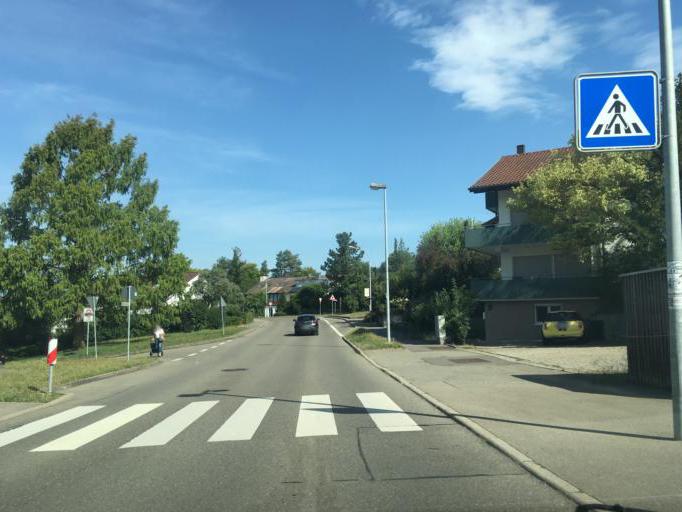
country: DE
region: Baden-Wuerttemberg
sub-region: Regierungsbezirk Stuttgart
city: Waldenbuch
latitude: 48.6429
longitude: 9.1396
